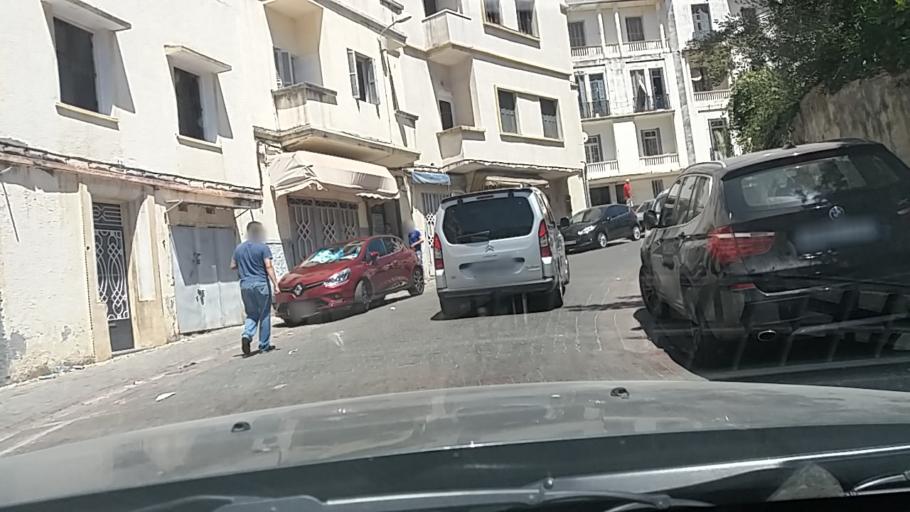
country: MA
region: Tanger-Tetouan
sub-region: Tanger-Assilah
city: Tangier
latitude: 35.7866
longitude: -5.8160
